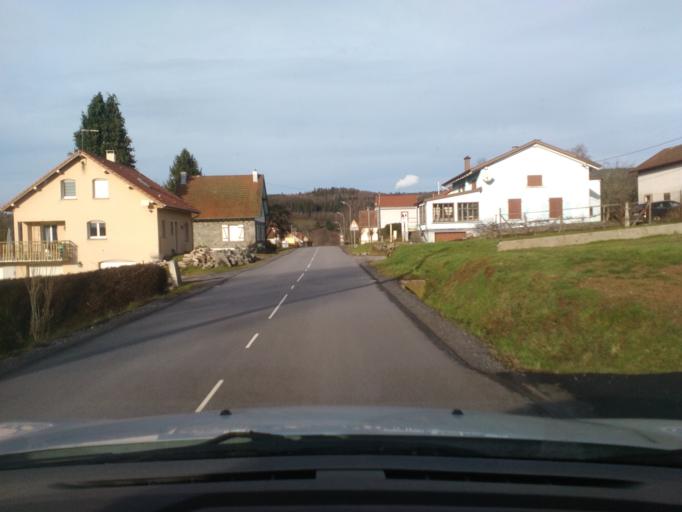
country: FR
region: Lorraine
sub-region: Departement des Vosges
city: Fraize
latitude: 48.1813
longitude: 6.9737
